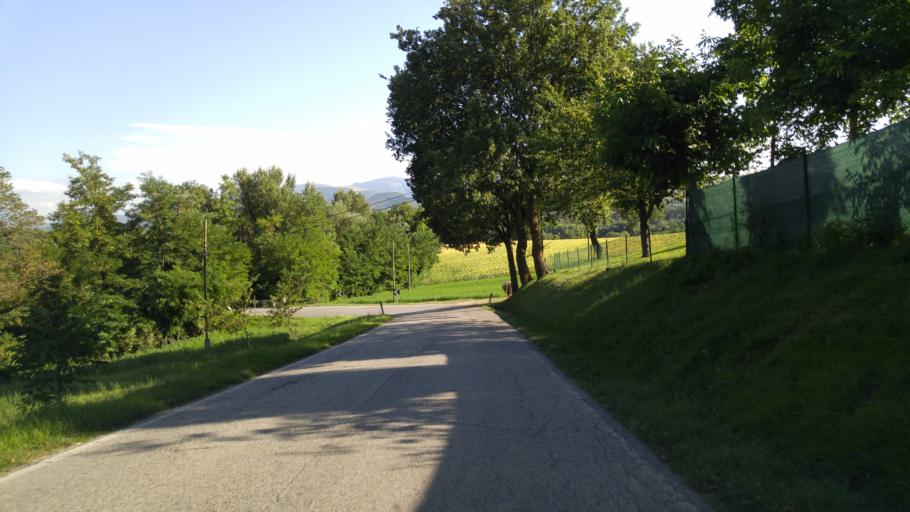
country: IT
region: The Marches
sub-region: Provincia di Pesaro e Urbino
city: Urbania
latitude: 43.6852
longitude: 12.5132
